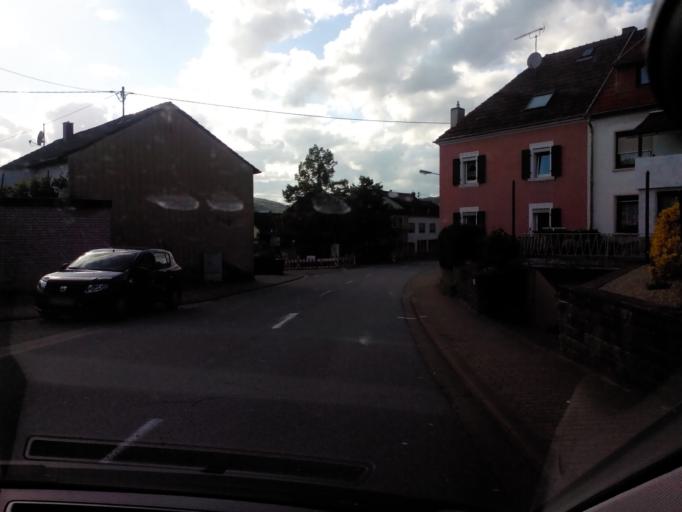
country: DE
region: Saarland
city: Rehlingen-Siersburg
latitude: 49.3655
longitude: 6.6658
